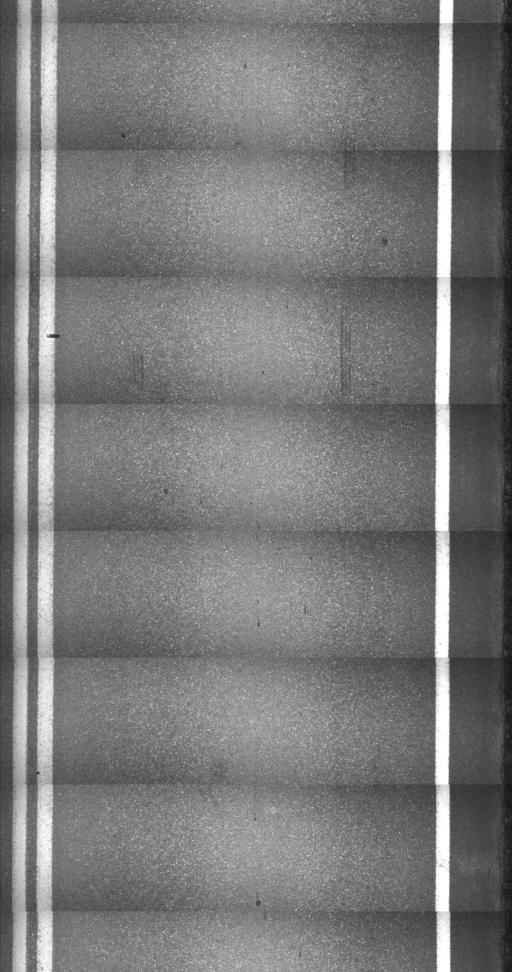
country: US
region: New York
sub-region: Clinton County
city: Cumberland Head
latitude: 44.6679
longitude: -73.3339
